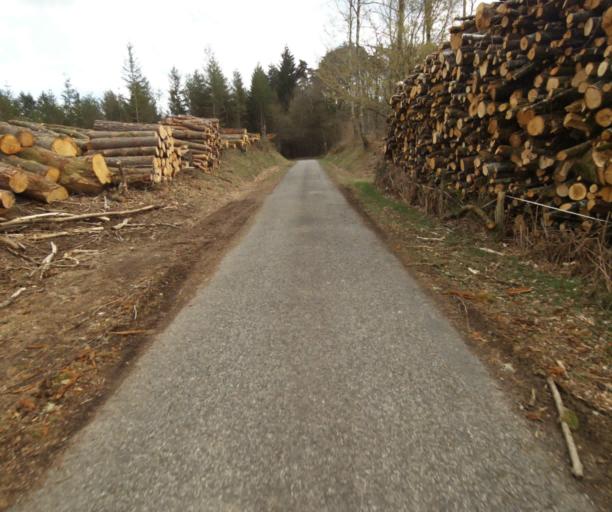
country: FR
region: Limousin
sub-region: Departement de la Correze
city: Argentat
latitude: 45.1934
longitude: 1.9281
